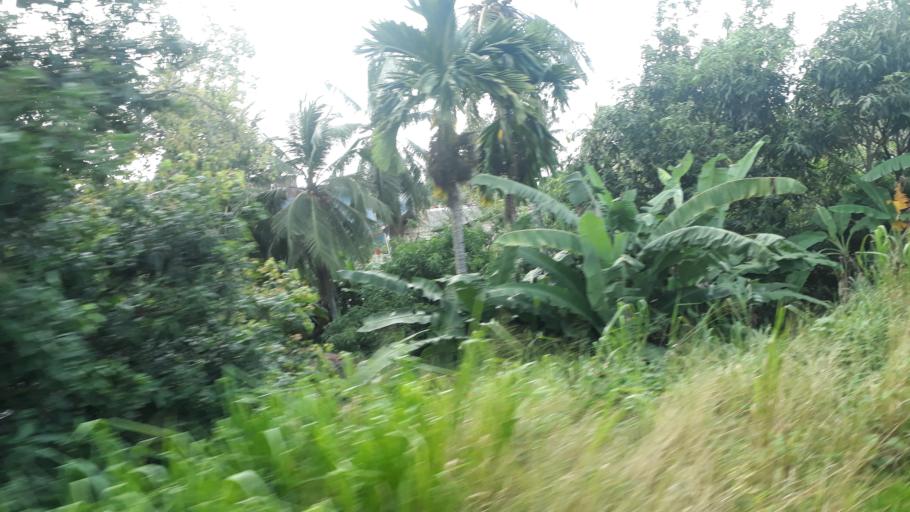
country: LK
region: Western
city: Peliyagoda
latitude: 6.9511
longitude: 79.8890
